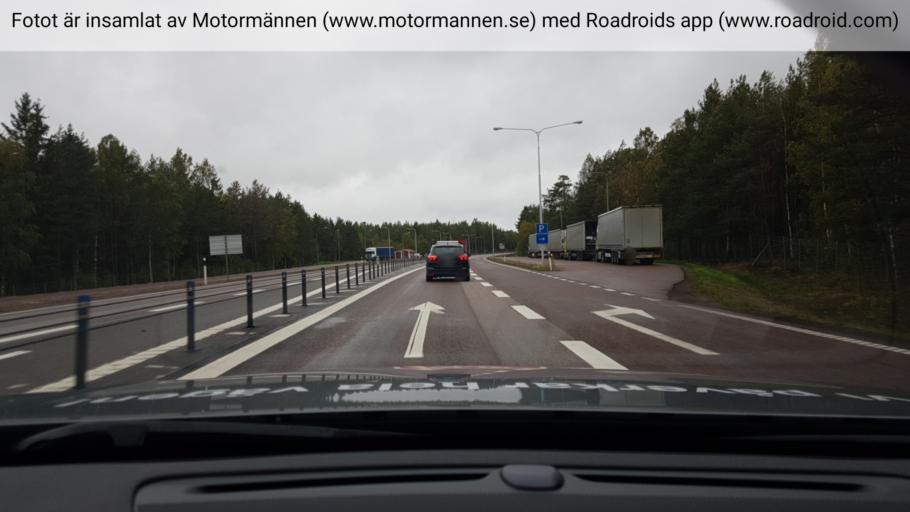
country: SE
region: Vaermland
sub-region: Kristinehamns Kommun
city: Kristinehamn
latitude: 59.3614
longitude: 14.0309
